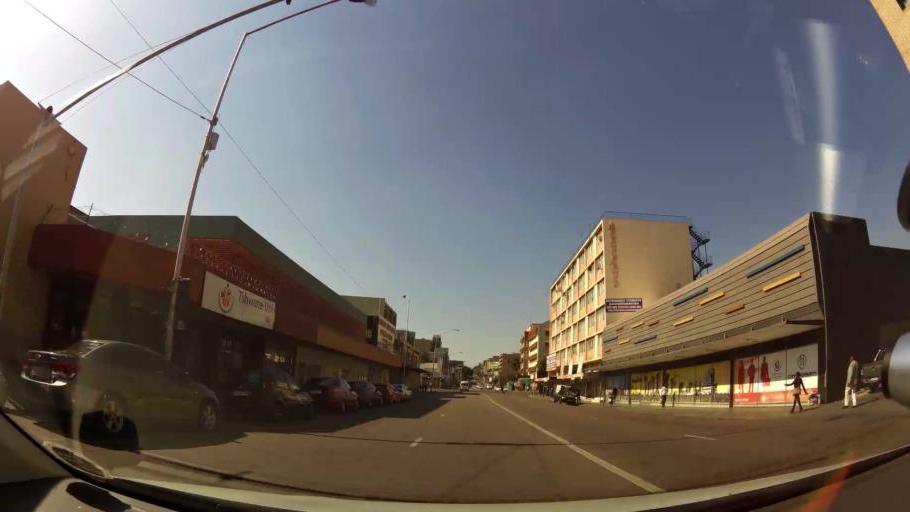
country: ZA
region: Gauteng
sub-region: City of Tshwane Metropolitan Municipality
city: Pretoria
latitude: -25.7457
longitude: 28.1993
